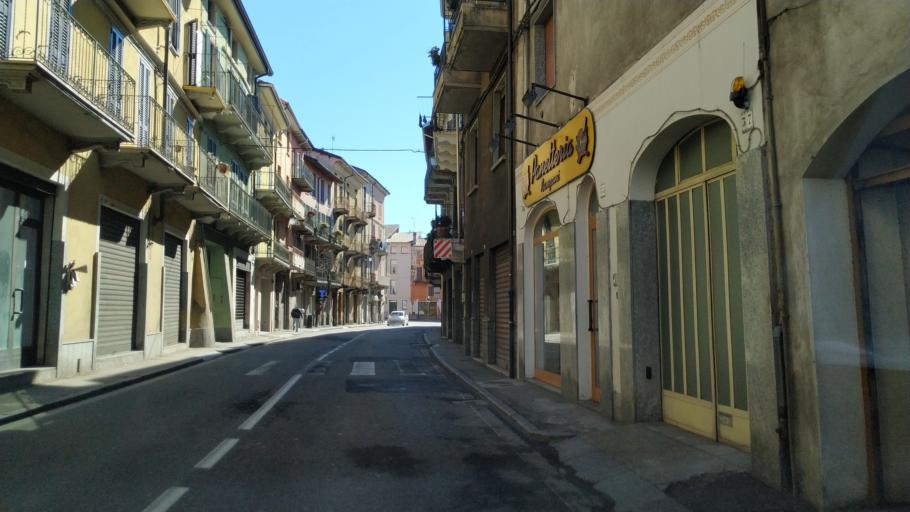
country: IT
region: Piedmont
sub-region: Provincia di Novara
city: Romagnano Sesia
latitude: 45.6351
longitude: 8.3806
